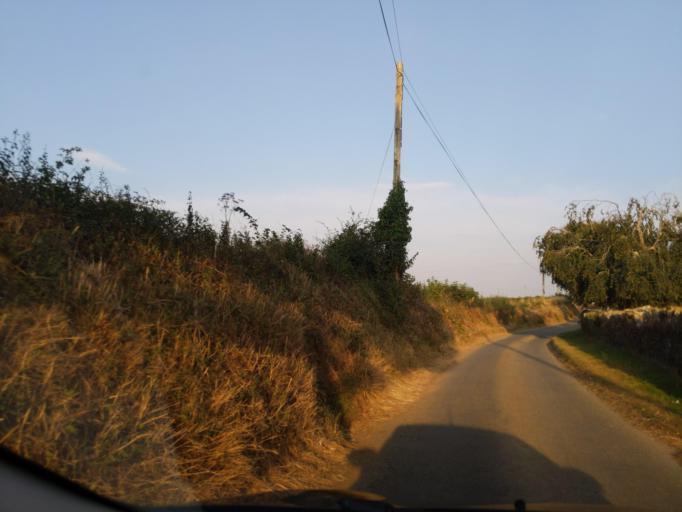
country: GB
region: England
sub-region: Cornwall
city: Fowey
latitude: 50.3683
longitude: -4.5915
